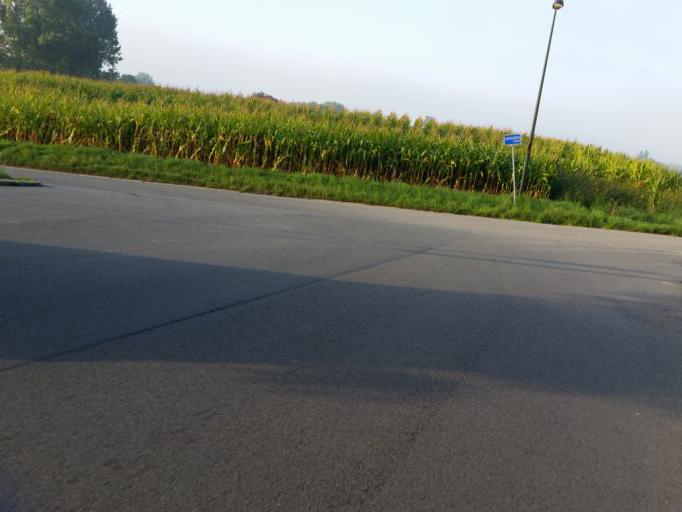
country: BE
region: Flanders
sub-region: Provincie Vlaams-Brabant
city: Grimbergen
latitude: 50.9032
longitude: 4.3800
